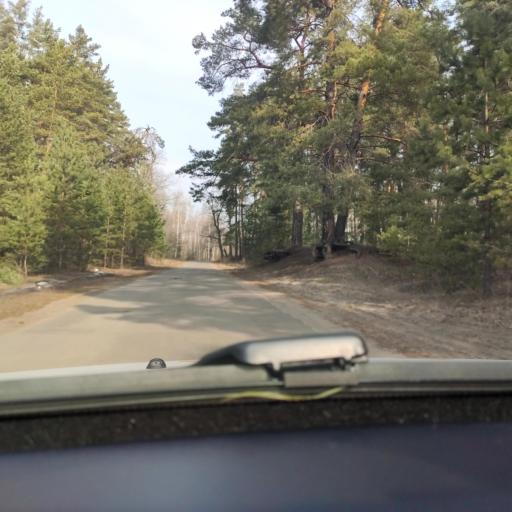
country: RU
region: Voronezj
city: Ramon'
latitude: 51.8919
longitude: 39.3689
